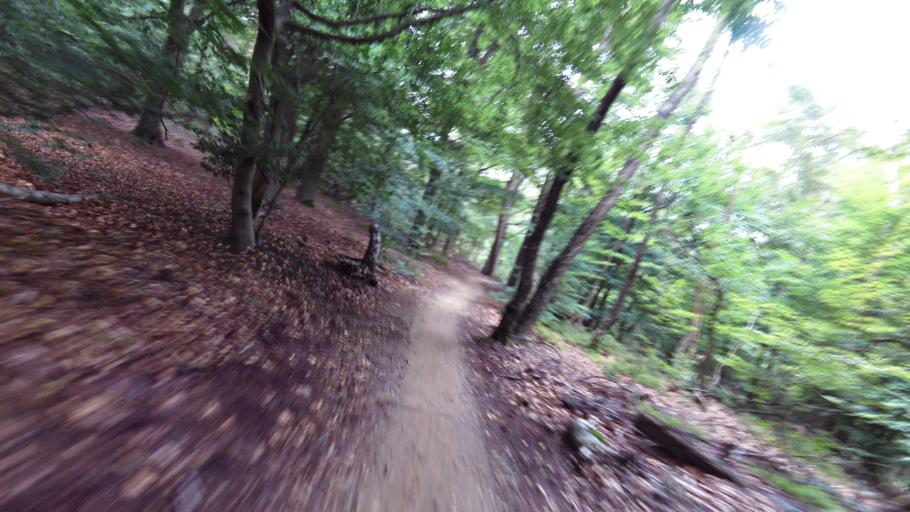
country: NL
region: Utrecht
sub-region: Gemeente Utrechtse Heuvelrug
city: Amerongen
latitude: 52.0086
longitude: 5.4734
